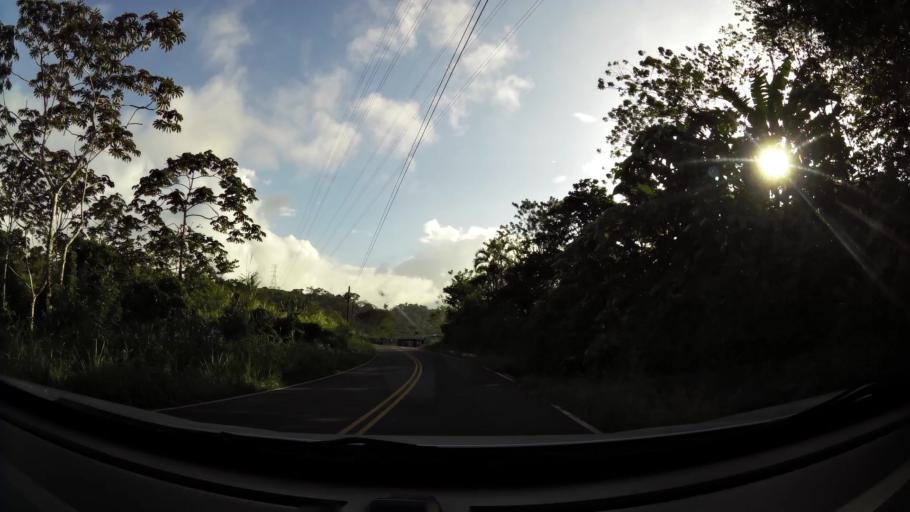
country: CR
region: Limon
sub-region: Canton de Siquirres
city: Siquirres
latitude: 10.0443
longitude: -83.5487
